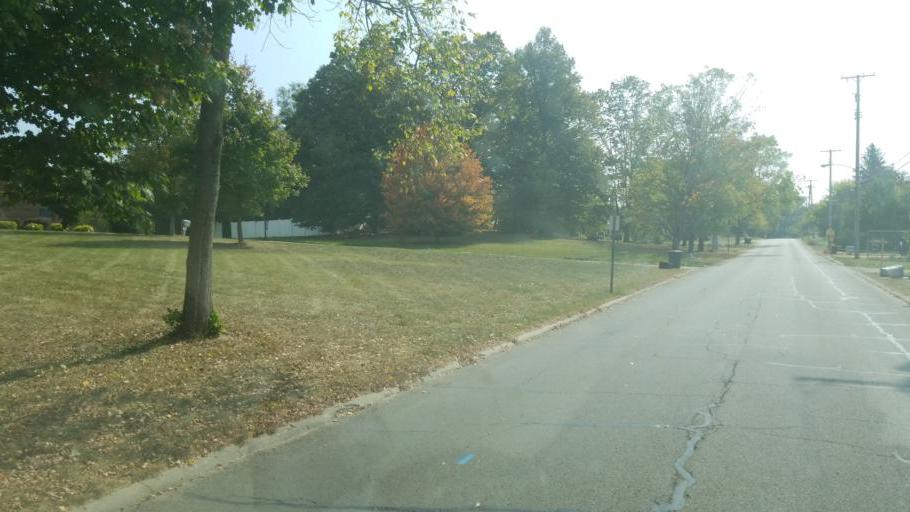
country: US
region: Ohio
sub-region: Morrow County
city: Mount Gilead
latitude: 40.5561
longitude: -82.8365
